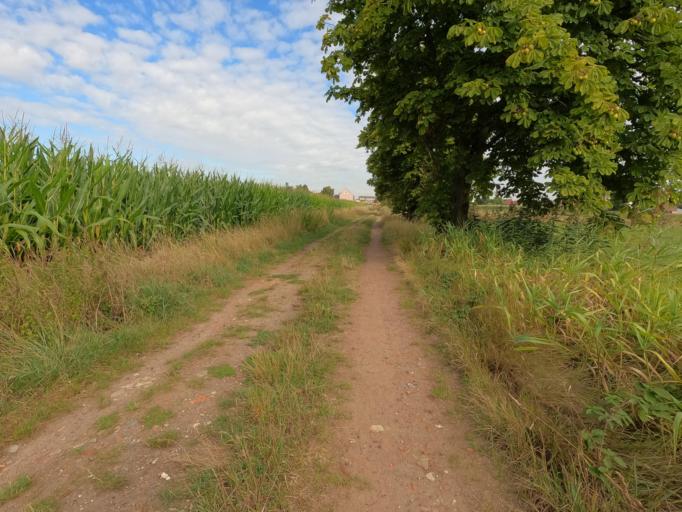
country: BE
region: Flanders
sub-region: Provincie Antwerpen
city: Kapellen
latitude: 51.3010
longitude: 4.4060
